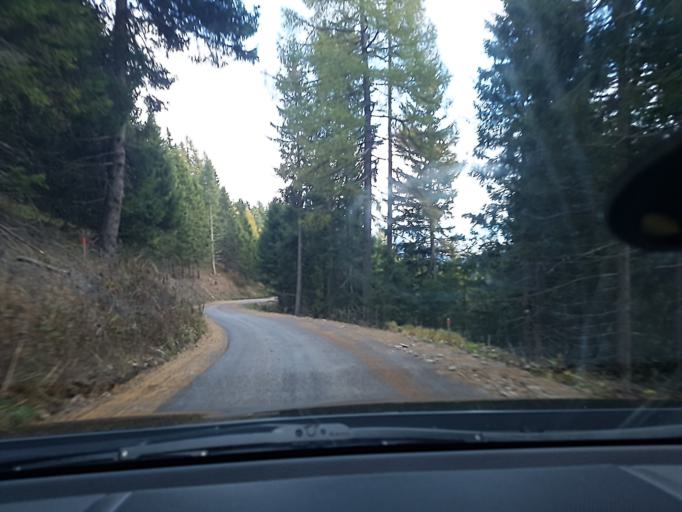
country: AT
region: Styria
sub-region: Politischer Bezirk Murtal
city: Oberzeiring
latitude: 47.2649
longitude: 14.4399
